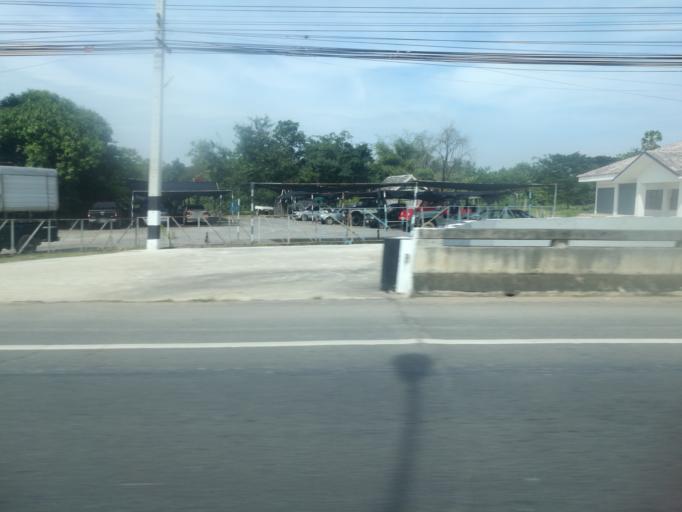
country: TH
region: Phetchaburi
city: Ban Lat
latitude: 13.0499
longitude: 99.9397
